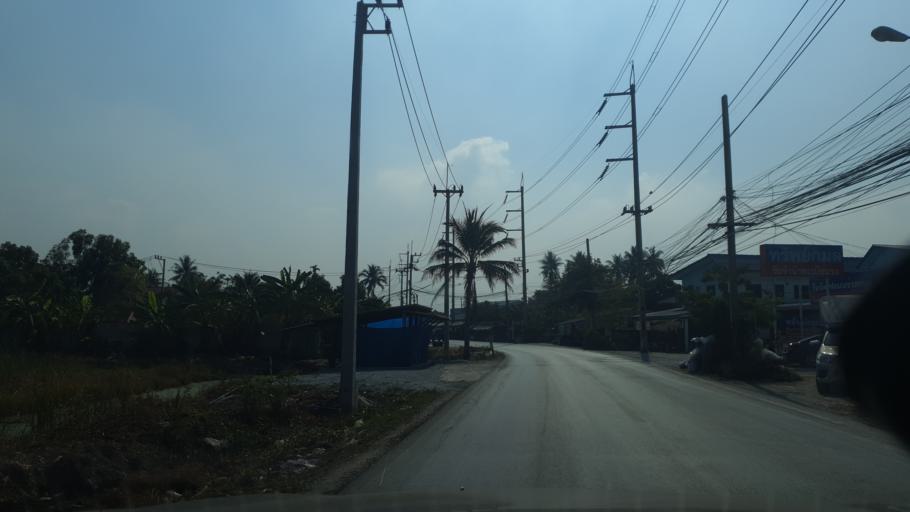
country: TH
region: Nakhon Pathom
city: Salaya
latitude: 13.7761
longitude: 100.2766
